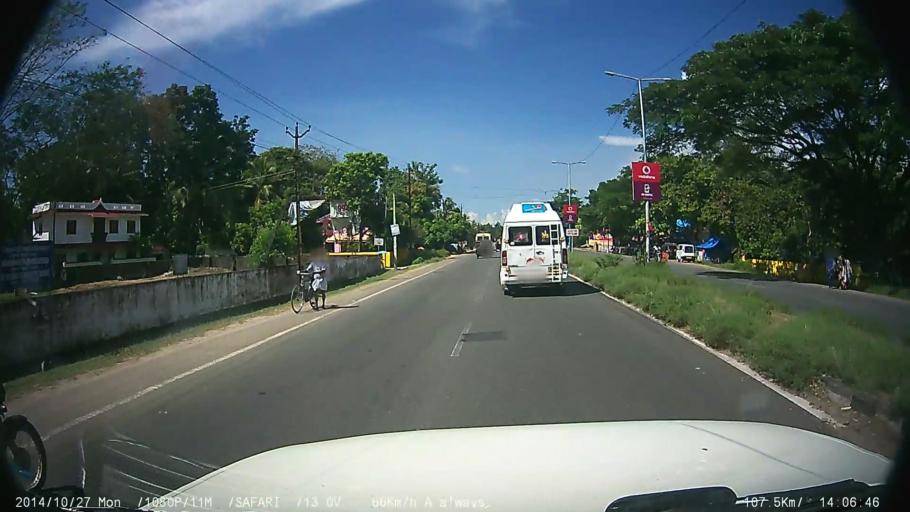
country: IN
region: Kerala
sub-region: Alappuzha
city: Kutiatodu
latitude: 9.7529
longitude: 76.3185
